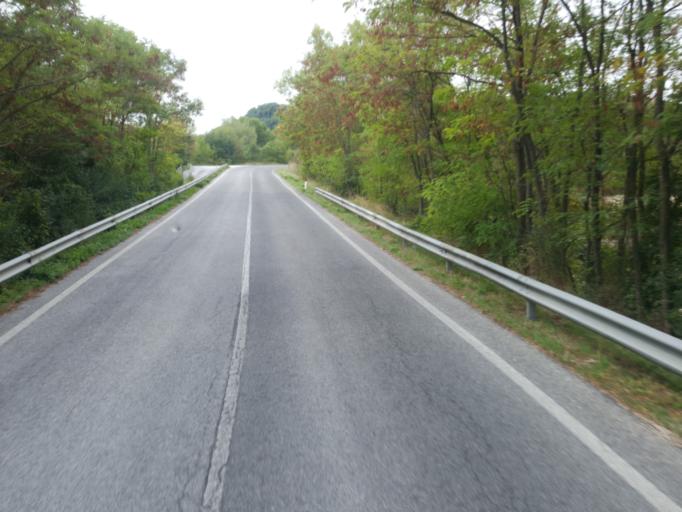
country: IT
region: The Marches
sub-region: Provincia di Ancona
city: Fabriano
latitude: 43.3327
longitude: 12.8312
